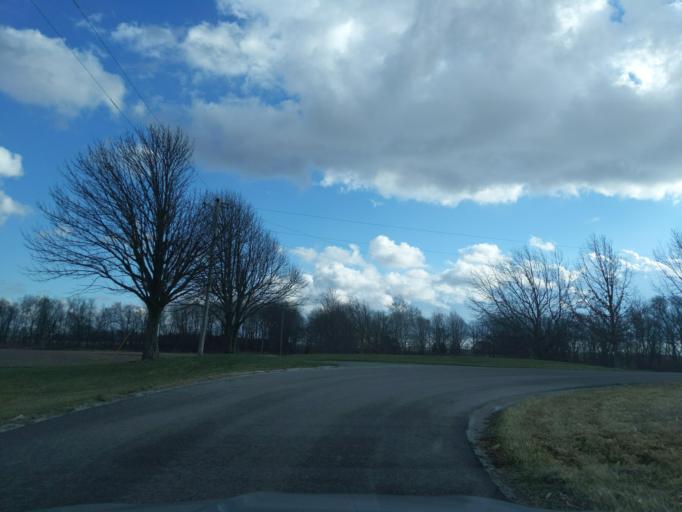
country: US
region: Indiana
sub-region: Decatur County
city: Greensburg
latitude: 39.3730
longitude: -85.4988
